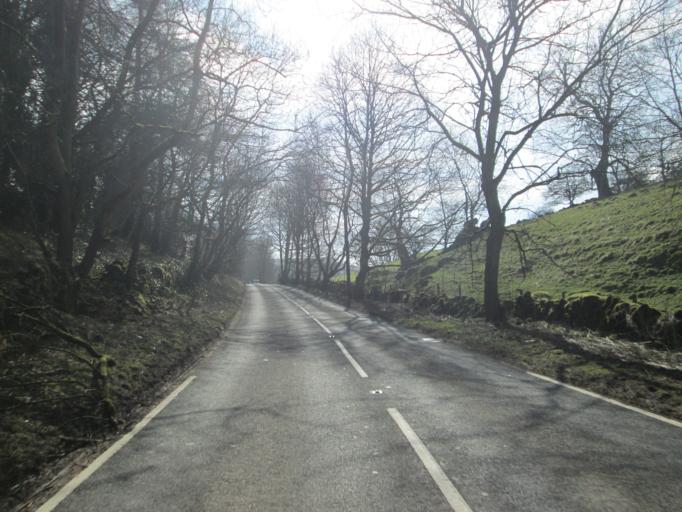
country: GB
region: England
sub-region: Derbyshire
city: Tideswell
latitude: 53.2470
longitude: -1.8078
